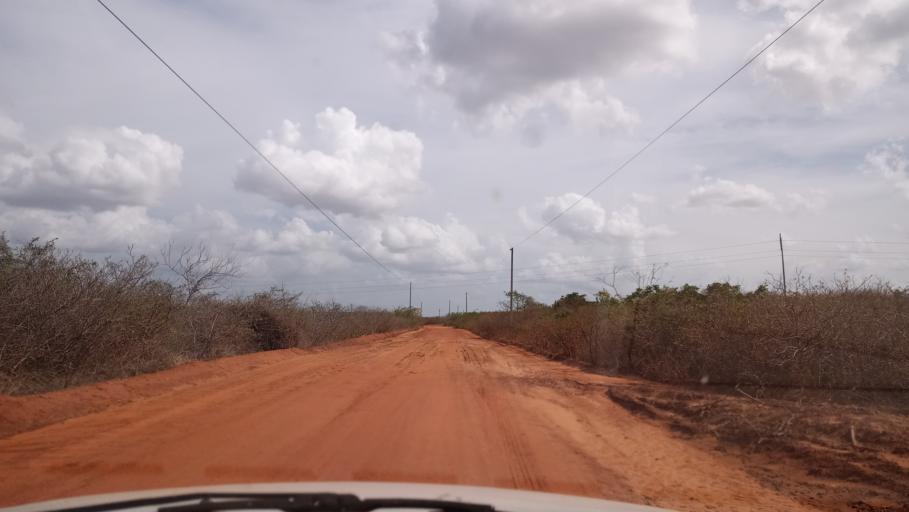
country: BR
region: Rio Grande do Norte
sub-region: Joao Camara
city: Joao Camara
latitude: -5.4744
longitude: -35.8275
